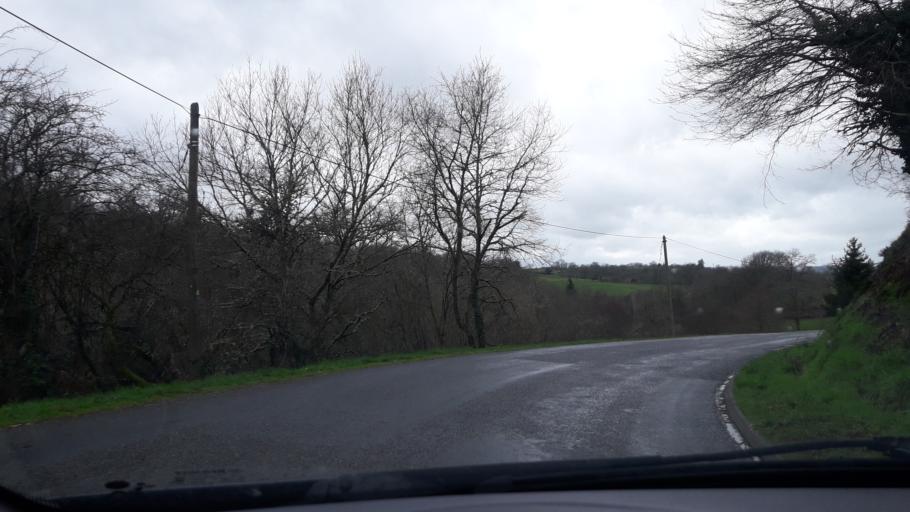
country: FR
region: Limousin
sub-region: Departement de la Haute-Vienne
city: Pierre-Buffiere
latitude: 45.7303
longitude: 1.3894
